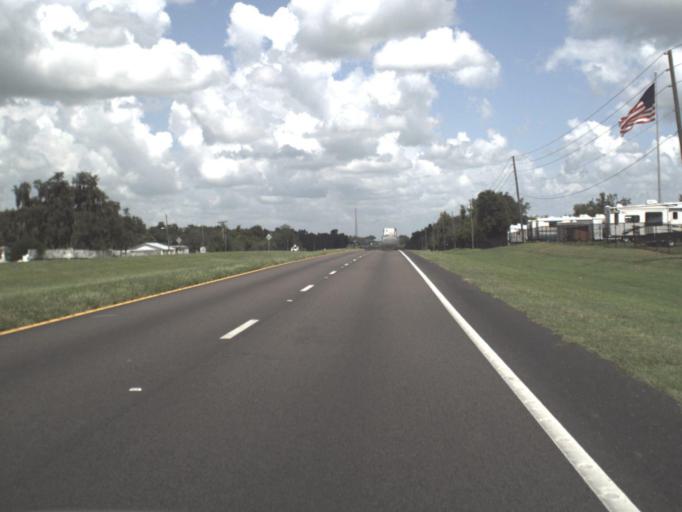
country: US
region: Florida
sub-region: Hardee County
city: Wauchula
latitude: 27.5868
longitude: -81.8200
